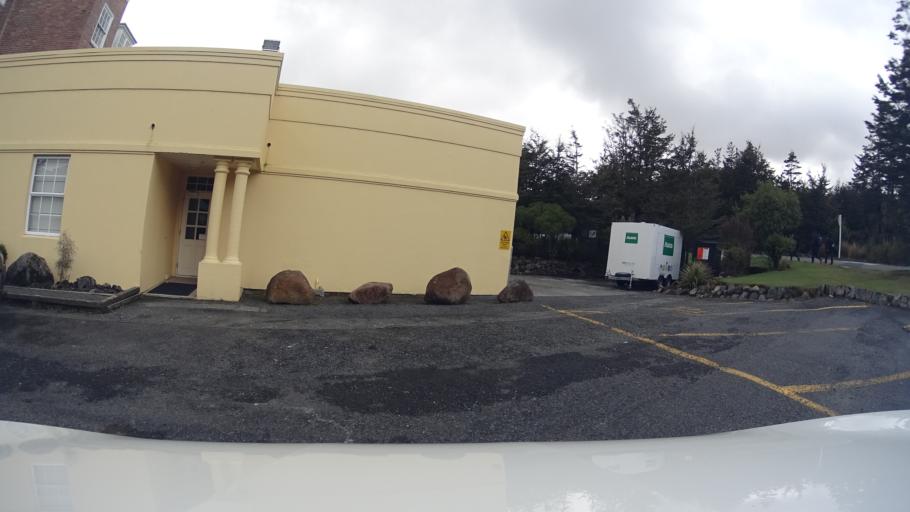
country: NZ
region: Manawatu-Wanganui
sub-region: Ruapehu District
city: Waiouru
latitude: -39.2003
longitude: 175.5392
